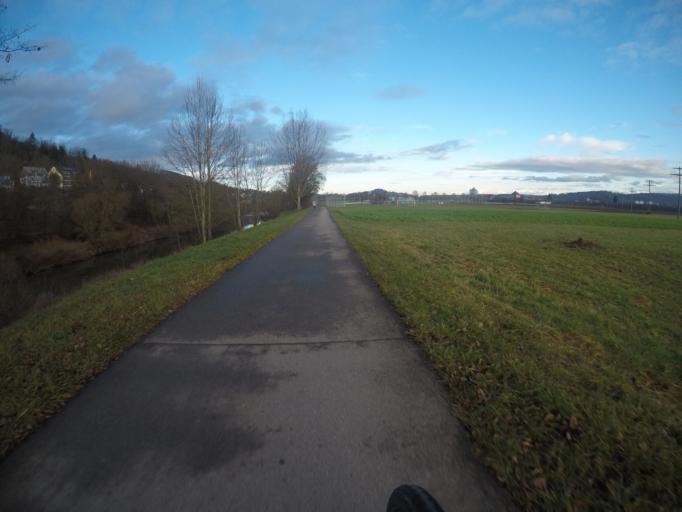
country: DE
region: Baden-Wuerttemberg
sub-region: Tuebingen Region
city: Tuebingen
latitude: 48.5072
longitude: 9.0333
